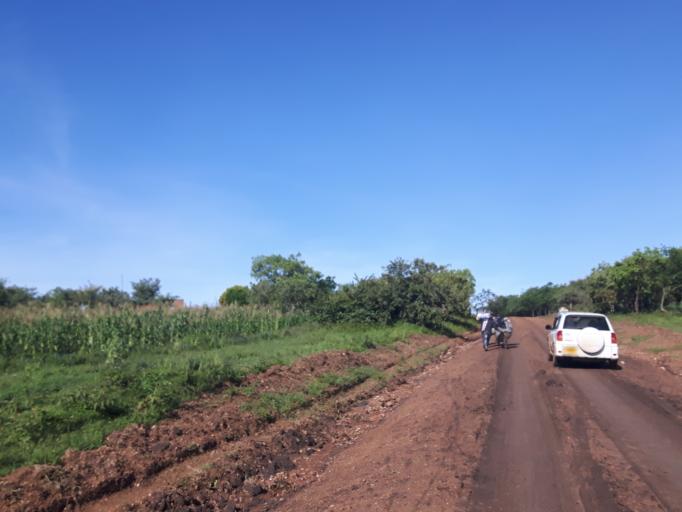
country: TZ
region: Mara
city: Mugumu
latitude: -1.9021
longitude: 34.5966
